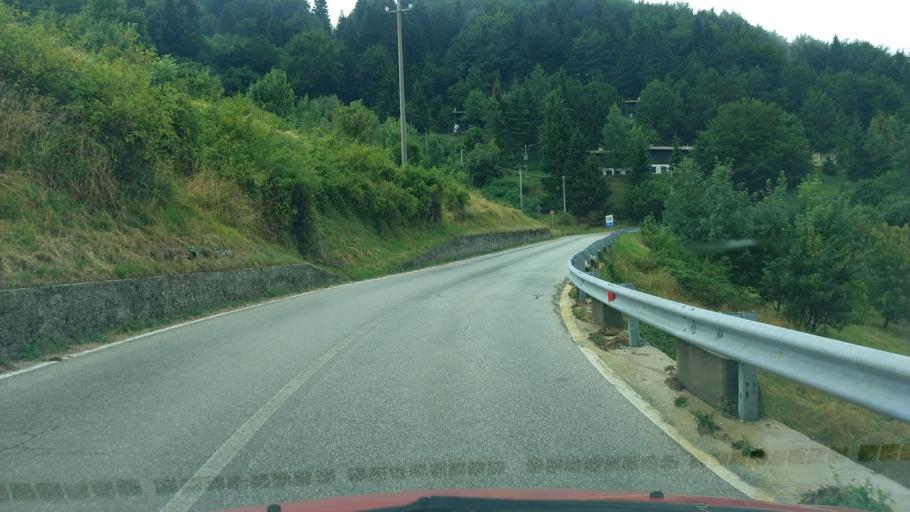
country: IT
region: Veneto
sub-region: Provincia di Vicenza
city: Tonezza del Cimone
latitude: 45.8665
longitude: 11.3328
